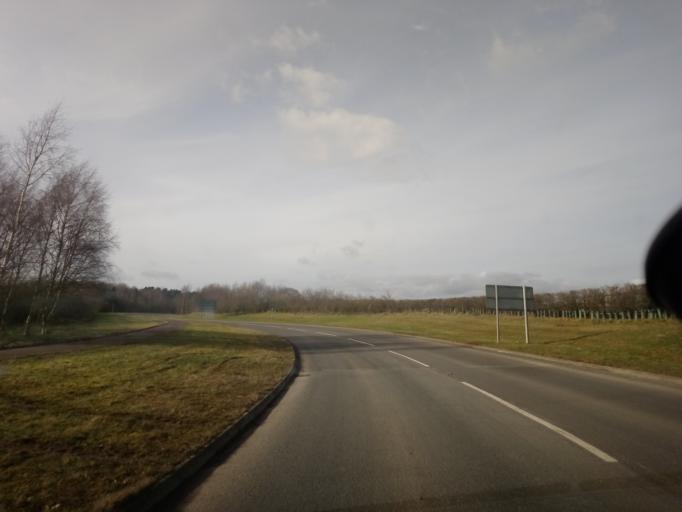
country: GB
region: England
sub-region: Shropshire
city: Stoke upon Tern
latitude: 52.8447
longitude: -2.5702
